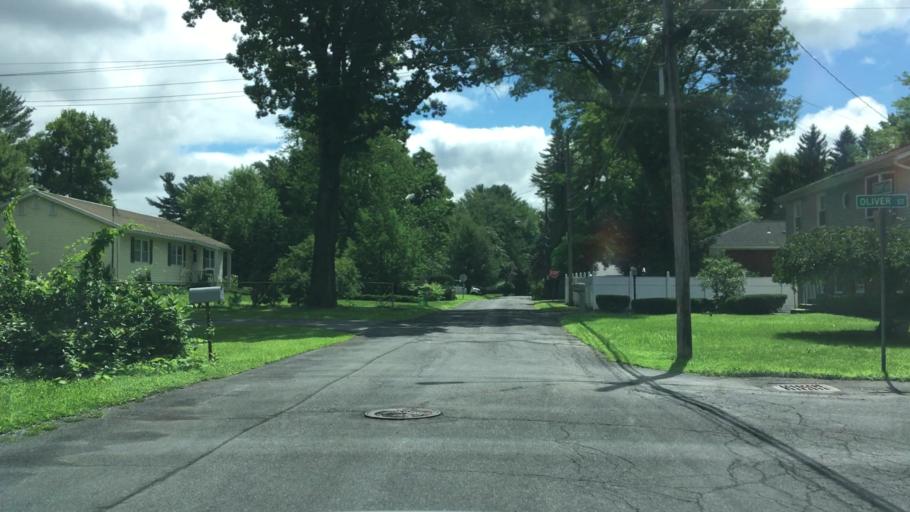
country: US
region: New York
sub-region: Schenectady County
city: Niskayuna
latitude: 42.7463
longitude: -73.8604
